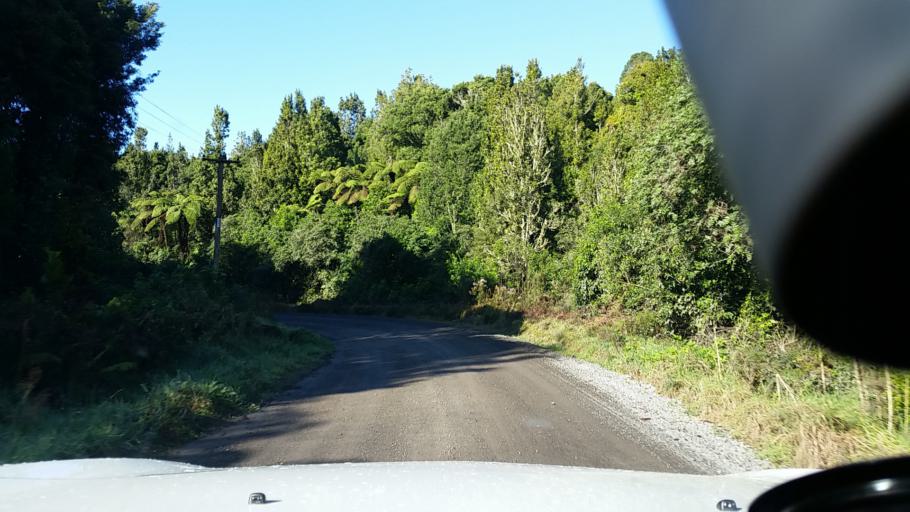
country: NZ
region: Bay of Plenty
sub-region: Kawerau District
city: Kawerau
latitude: -38.0187
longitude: 176.4697
